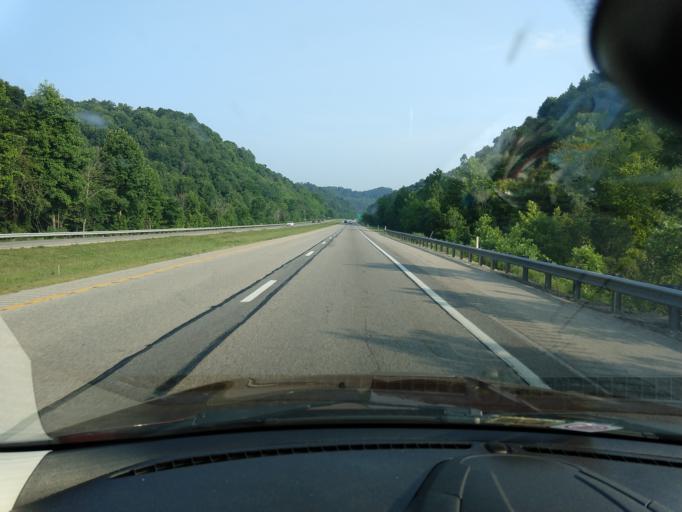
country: US
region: West Virginia
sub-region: Kanawha County
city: Sissonville
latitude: 38.4498
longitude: -81.6333
